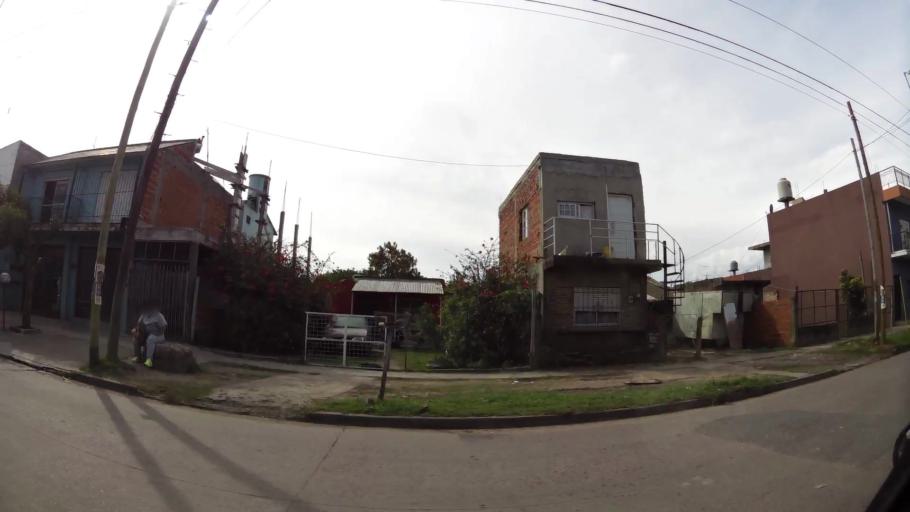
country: AR
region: Buenos Aires
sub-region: Partido de Quilmes
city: Quilmes
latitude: -34.7675
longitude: -58.2554
